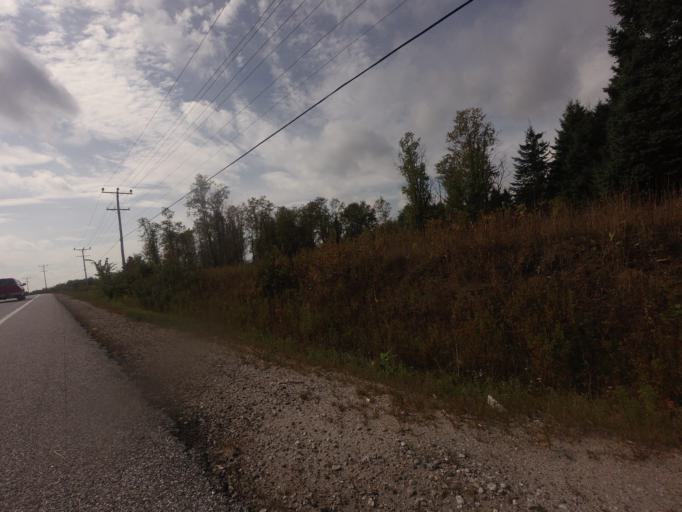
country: CA
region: Quebec
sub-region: Outaouais
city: Wakefield
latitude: 45.8828
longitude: -76.0277
